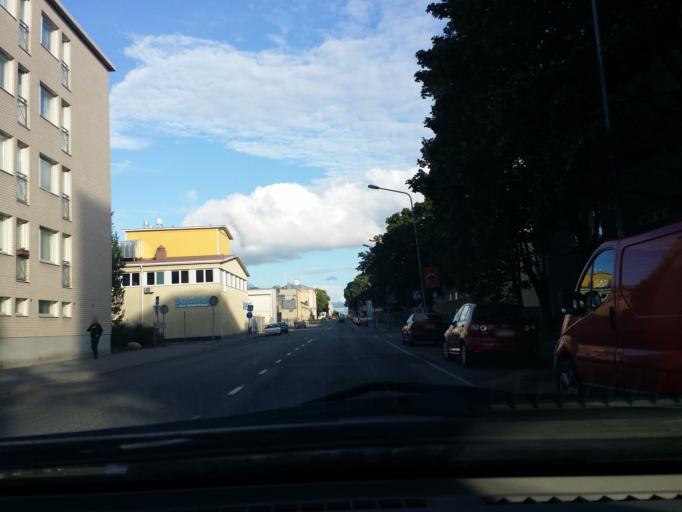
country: FI
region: Satakunta
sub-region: Pori
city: Pori
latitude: 61.4891
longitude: 21.7860
